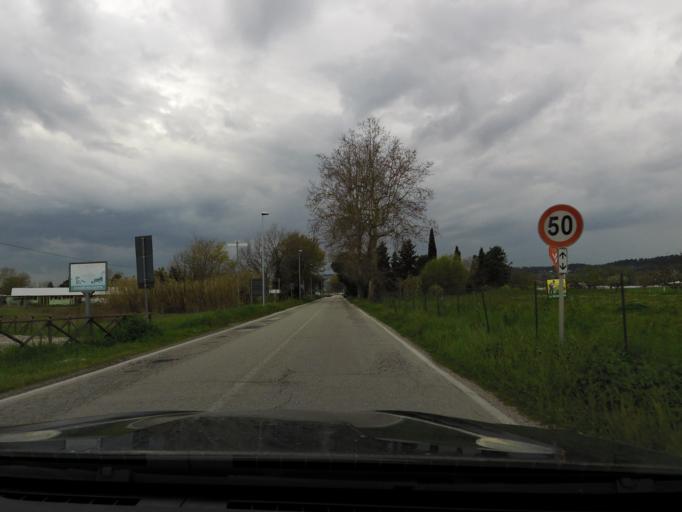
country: IT
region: The Marches
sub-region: Provincia di Ancona
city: Villa Musone
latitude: 43.4480
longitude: 13.6056
